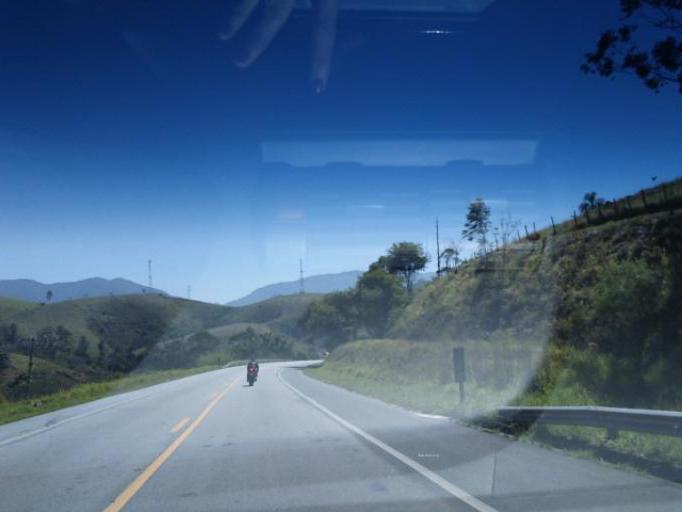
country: BR
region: Sao Paulo
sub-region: Tremembe
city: Tremembe
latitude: -22.9047
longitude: -45.5878
